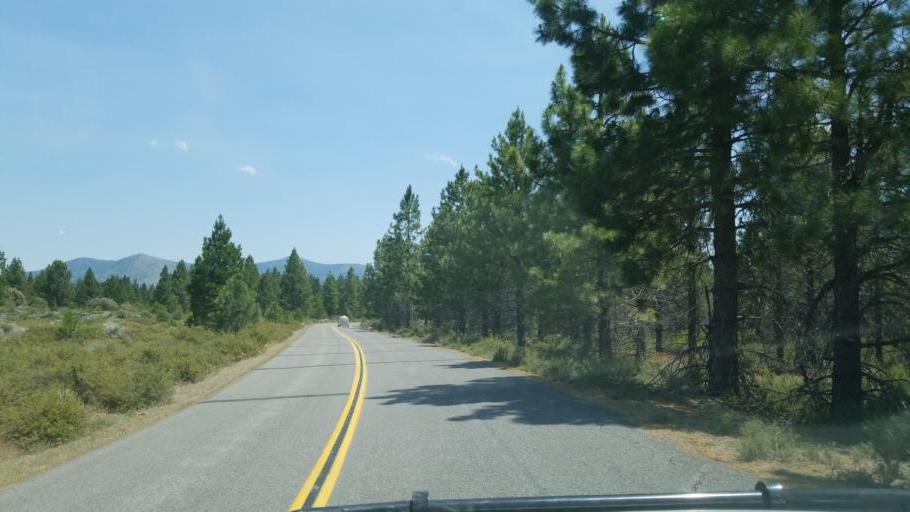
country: US
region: California
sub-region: Lassen County
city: Susanville
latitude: 40.5777
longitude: -120.8471
